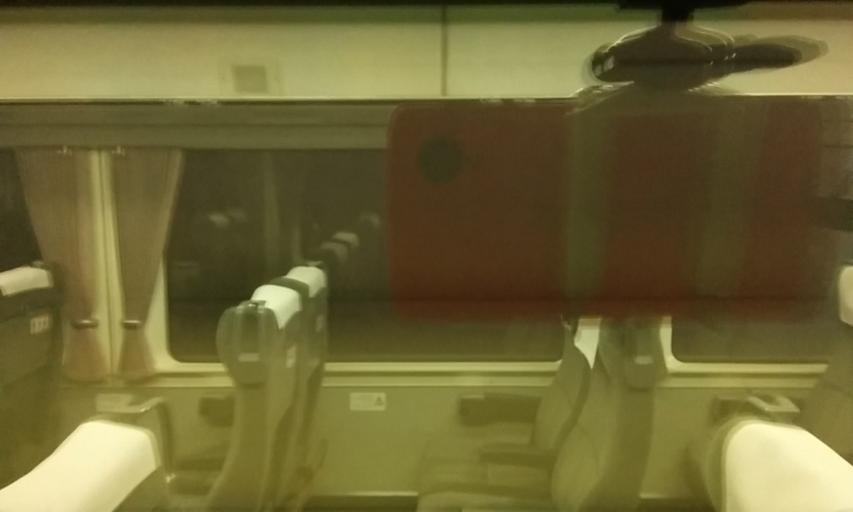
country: JP
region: Nagano
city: Hotaka
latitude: 36.3954
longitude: 138.0050
